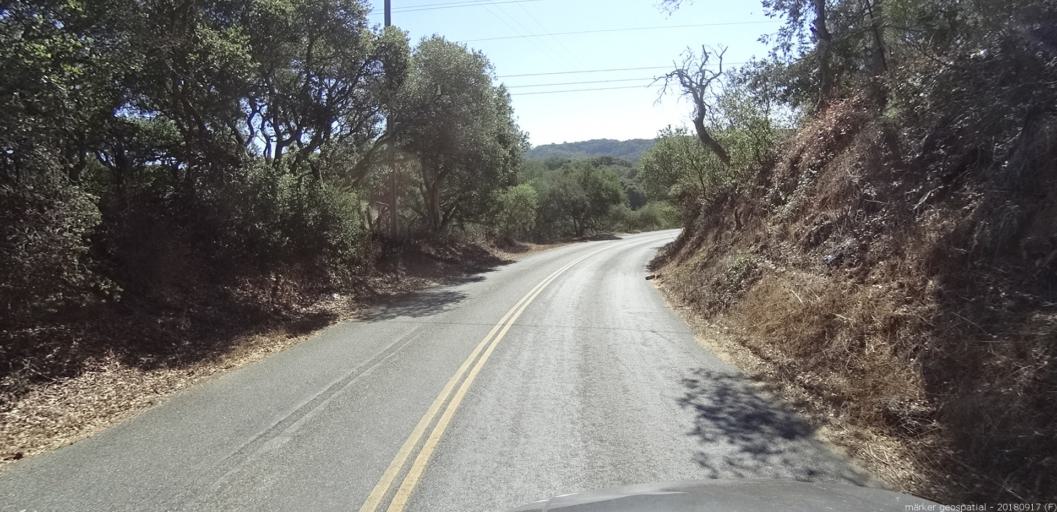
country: US
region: California
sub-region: Monterey County
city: Elkhorn
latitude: 36.8376
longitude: -121.6979
